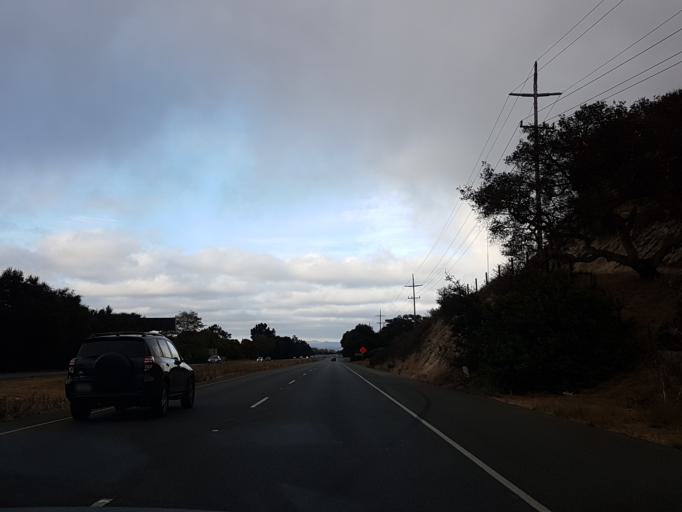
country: US
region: California
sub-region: Monterey County
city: Salinas
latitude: 36.6128
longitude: -121.6897
